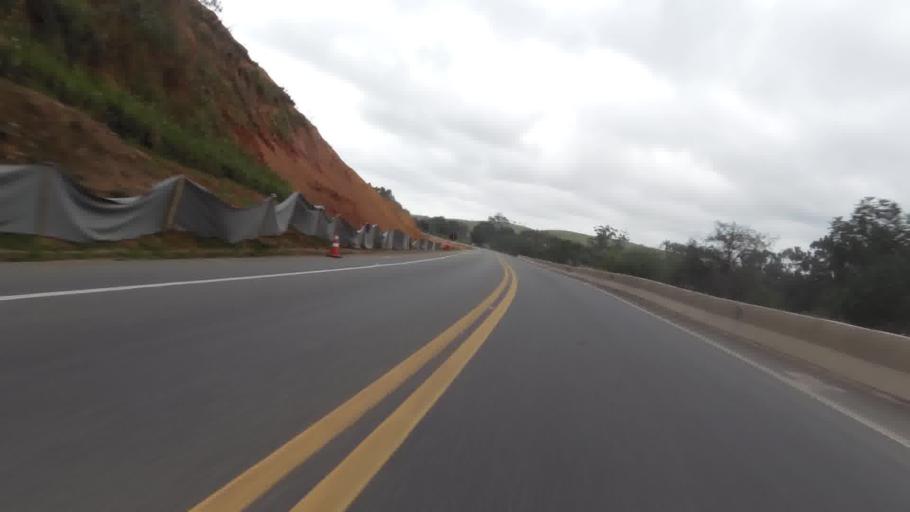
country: BR
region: Espirito Santo
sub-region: Iconha
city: Iconha
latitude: -20.7368
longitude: -40.7604
